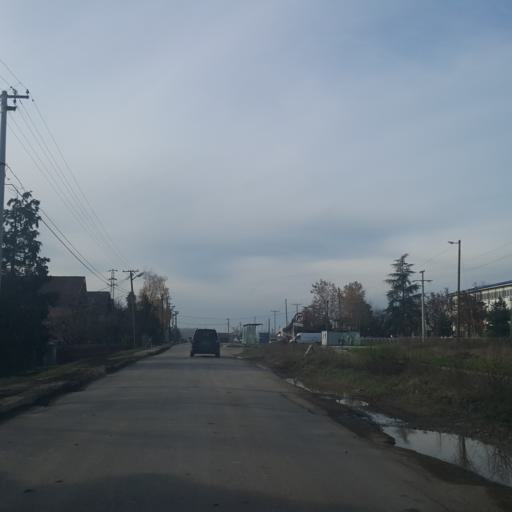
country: RS
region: Central Serbia
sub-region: Belgrade
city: Lazarevac
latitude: 44.3986
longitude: 20.3721
